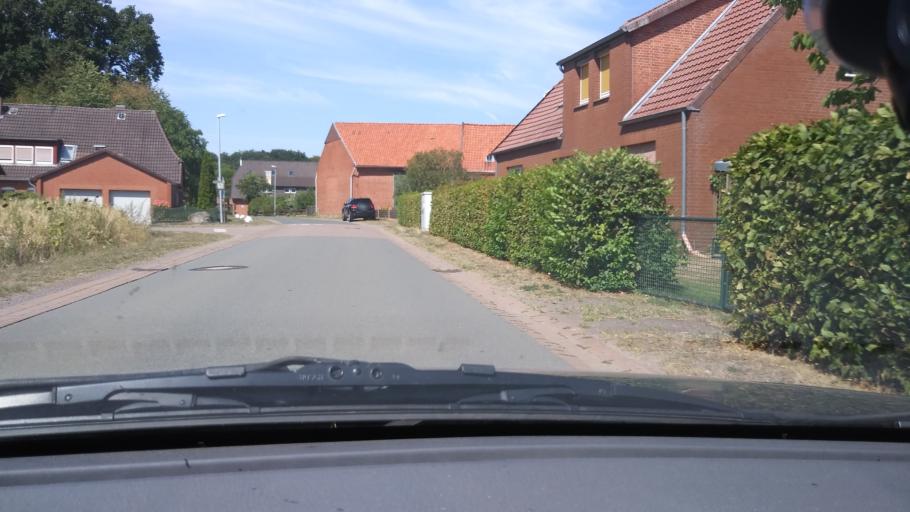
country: DE
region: Lower Saxony
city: Binnen
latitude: 52.6202
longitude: 9.1271
